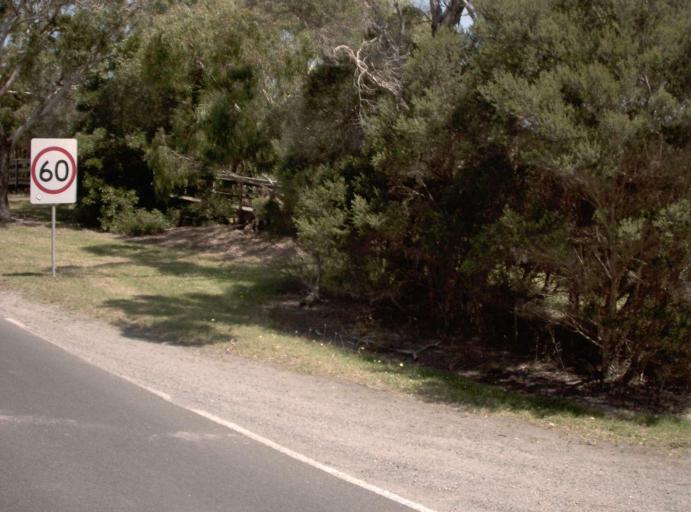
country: AU
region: Victoria
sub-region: Bass Coast
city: North Wonthaggi
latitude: -38.7017
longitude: 145.8730
